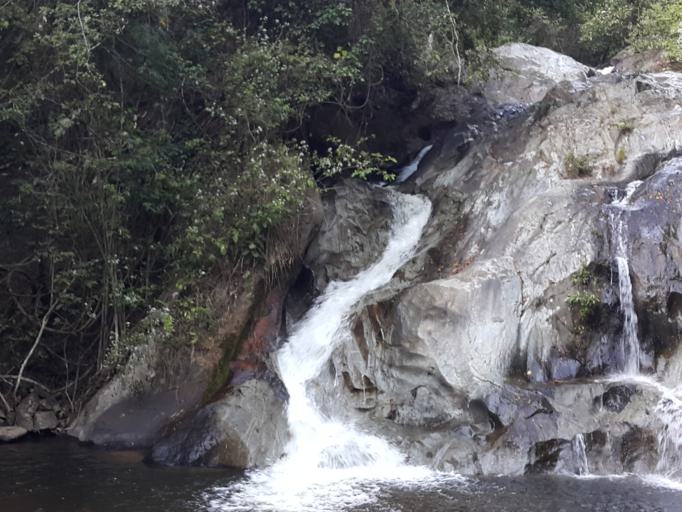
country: TH
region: Chiang Mai
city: Wiang Haeng
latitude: 19.6290
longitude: 98.5750
